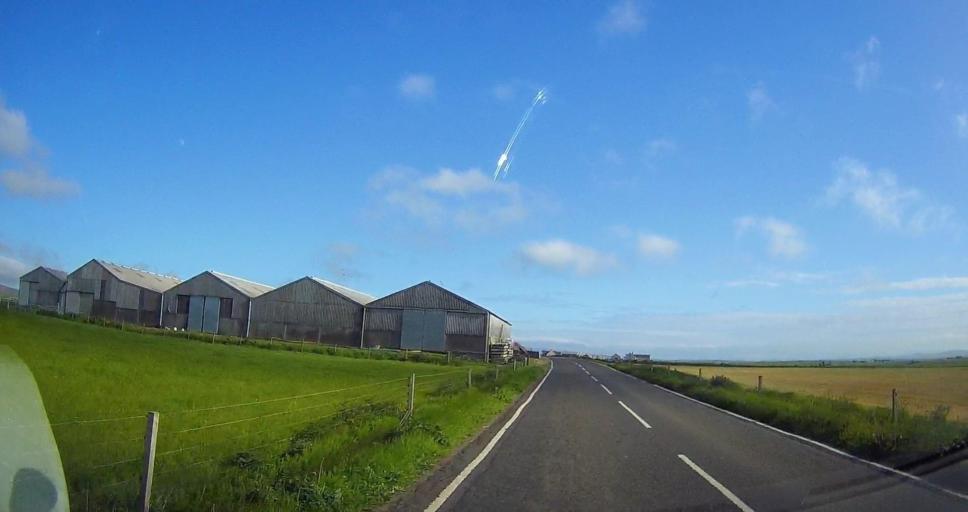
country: GB
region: Scotland
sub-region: Orkney Islands
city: Stromness
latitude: 59.0833
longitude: -3.2545
